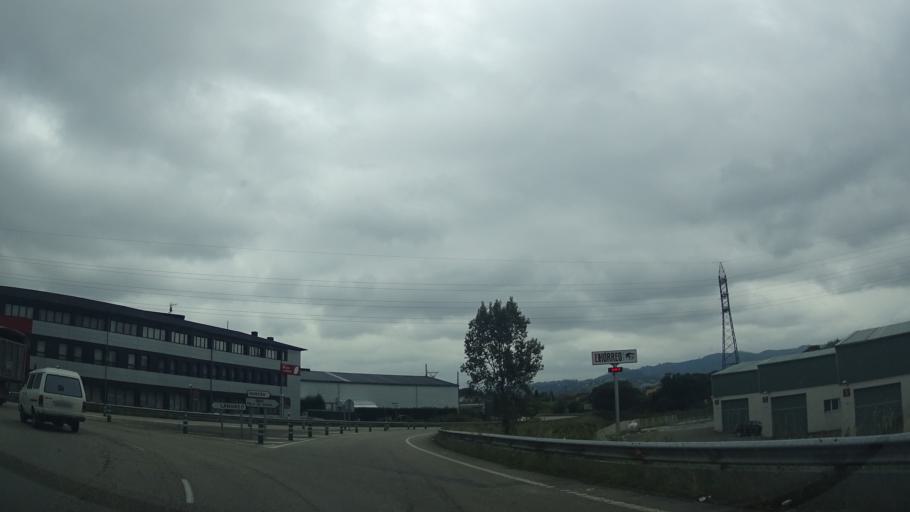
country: ES
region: Asturias
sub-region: Province of Asturias
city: Norena
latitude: 43.3825
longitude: -5.7459
